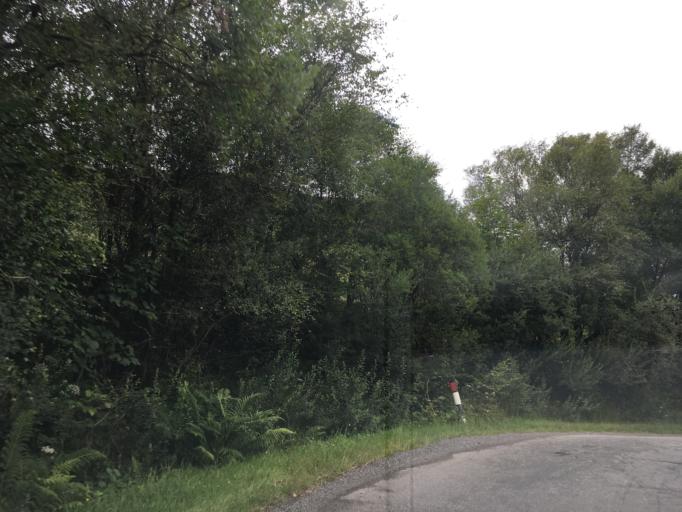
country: GB
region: Scotland
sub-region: Argyll and Bute
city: Oban
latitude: 56.3810
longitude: -5.1846
